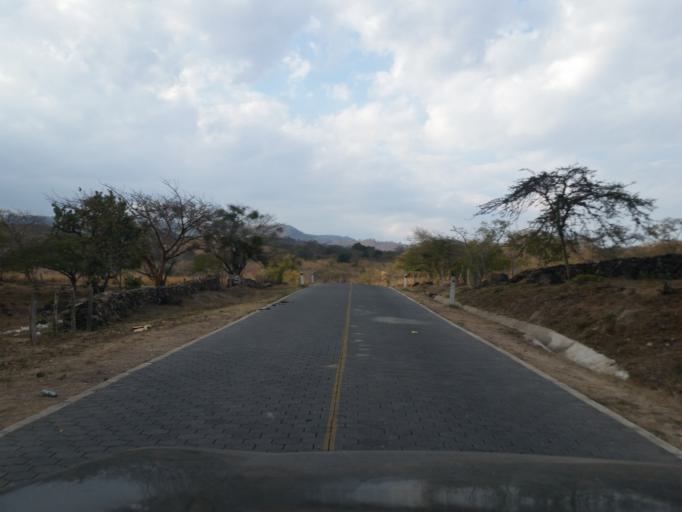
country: NI
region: Jinotega
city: La Concordia
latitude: 13.1841
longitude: -86.1692
